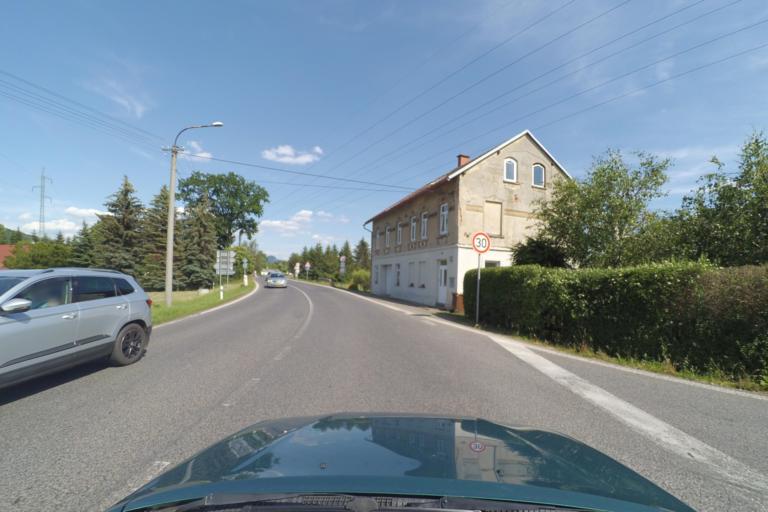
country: CZ
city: Zakupy
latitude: 50.6786
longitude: 14.6507
